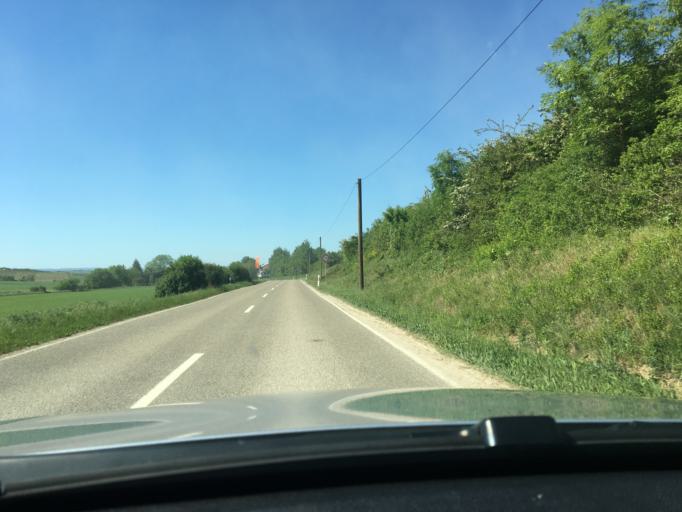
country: DE
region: Rheinland-Pfalz
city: Eckelsheim
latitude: 49.7854
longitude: 7.9856
